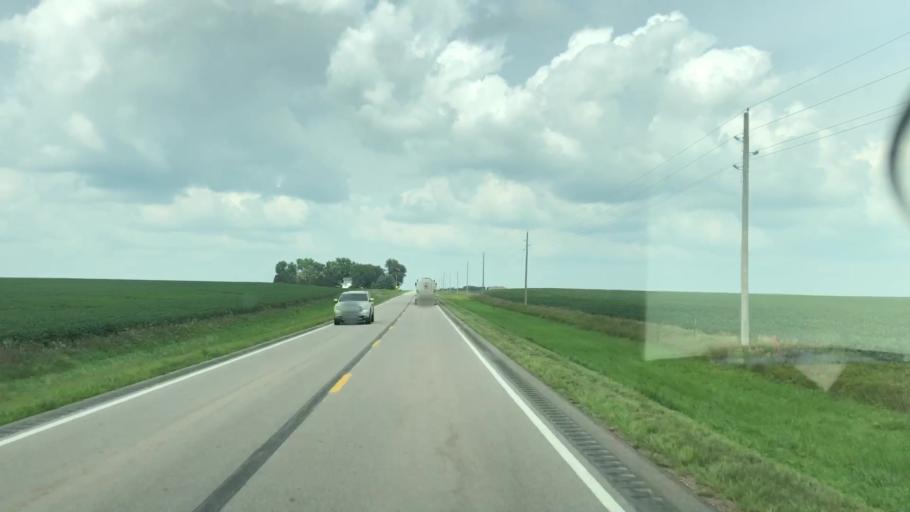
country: US
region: Iowa
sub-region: Plymouth County
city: Remsen
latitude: 42.7861
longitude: -95.9578
